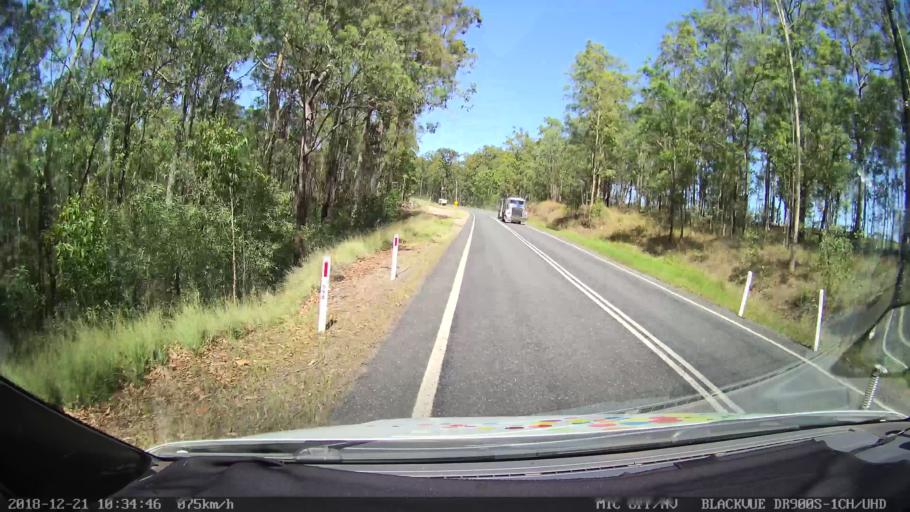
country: AU
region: New South Wales
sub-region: Clarence Valley
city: South Grafton
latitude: -29.6163
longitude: 152.6517
